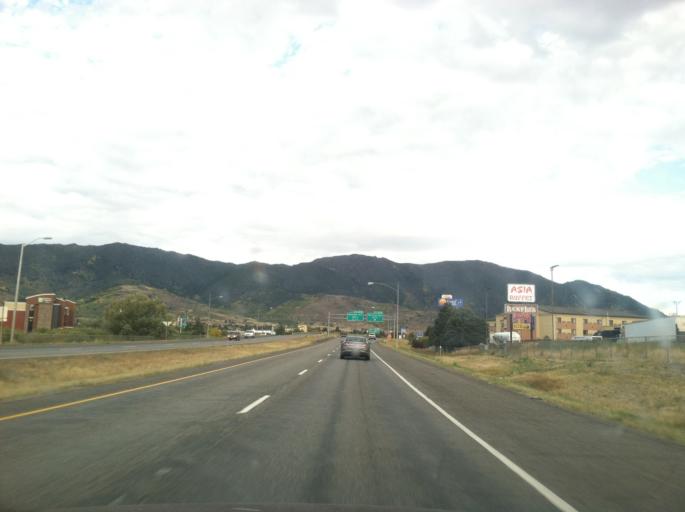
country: US
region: Montana
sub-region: Silver Bow County
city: Butte
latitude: 45.9858
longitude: -112.5139
